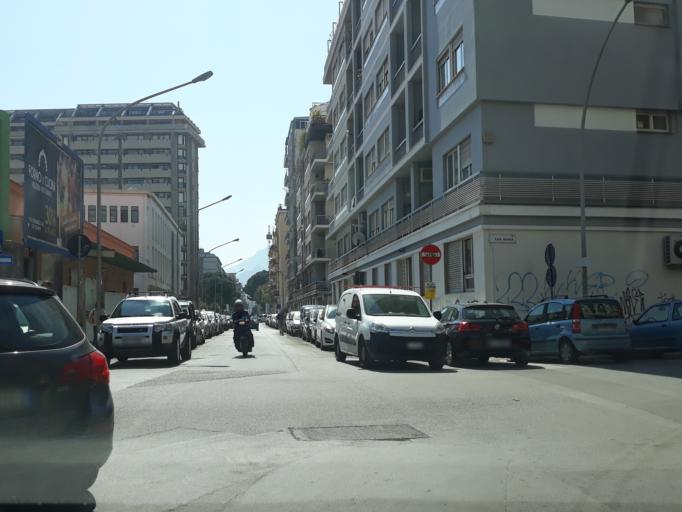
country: IT
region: Sicily
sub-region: Palermo
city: Palermo
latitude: 38.1358
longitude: 13.3526
